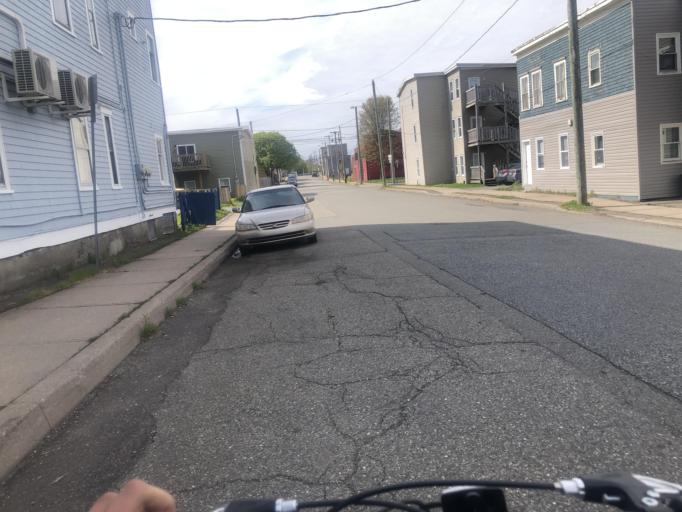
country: CA
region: New Brunswick
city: Saint John
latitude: 45.2782
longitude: -66.0815
